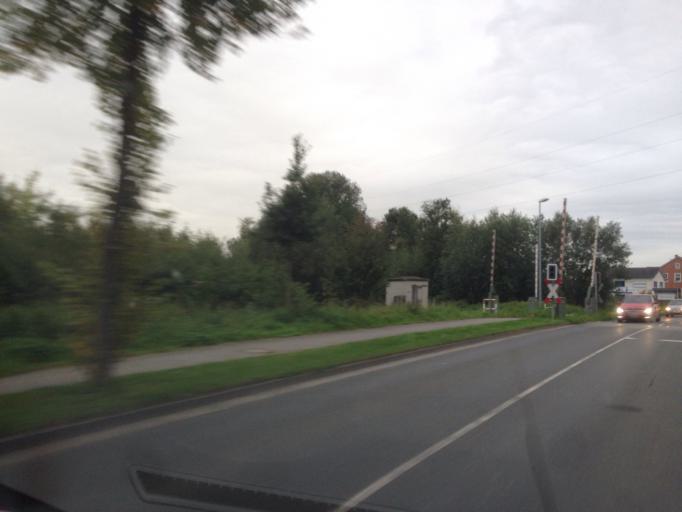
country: DE
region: North Rhine-Westphalia
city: Ludinghausen
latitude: 51.7587
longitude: 7.4342
